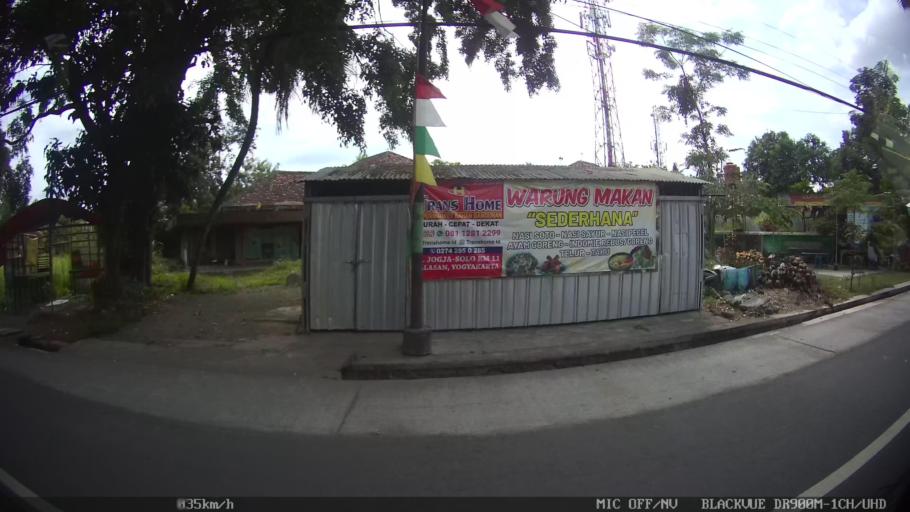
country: ID
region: Central Java
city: Candi Prambanan
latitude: -7.7642
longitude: 110.4739
